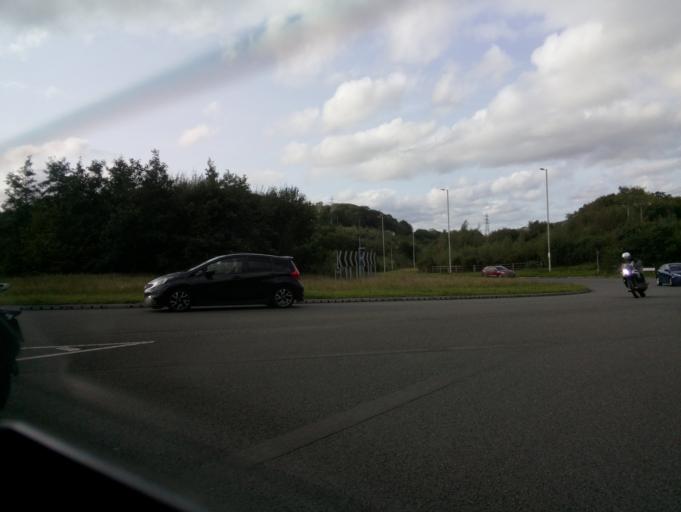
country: GB
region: Wales
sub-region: Rhondda Cynon Taf
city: Llantwit Fardre
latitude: 51.5701
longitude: -3.3033
